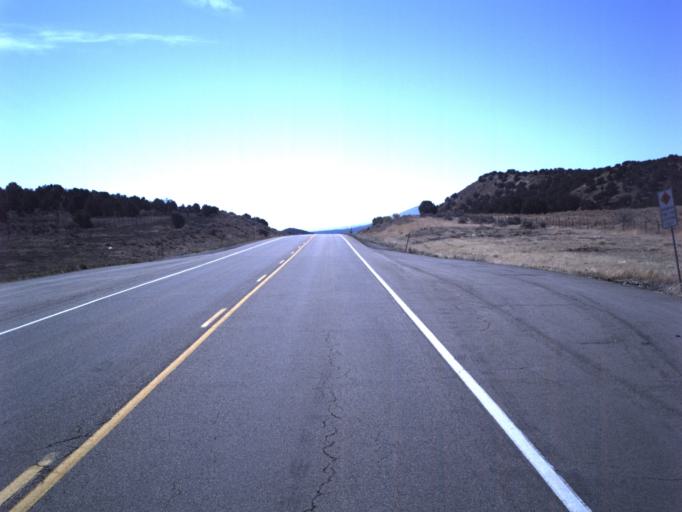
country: US
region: Utah
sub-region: Sanpete County
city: Gunnison
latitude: 39.3908
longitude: -111.9279
